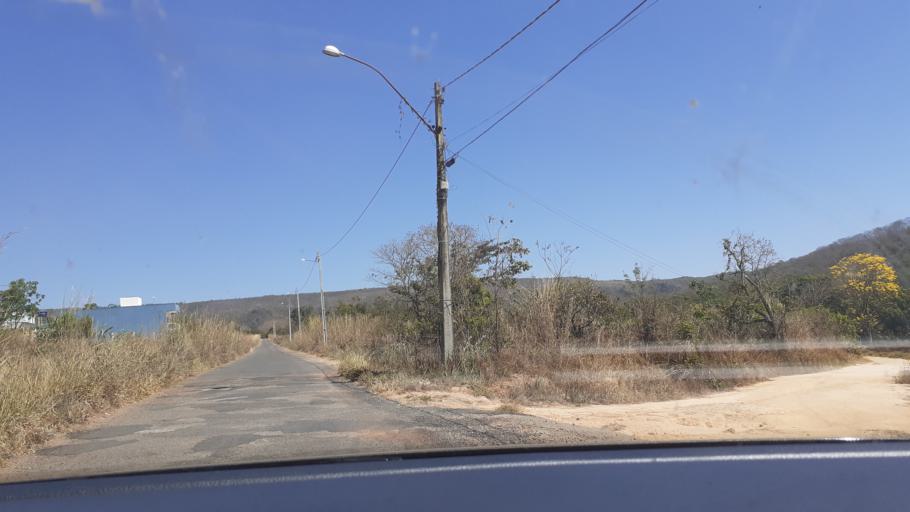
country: BR
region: Goias
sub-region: Caldas Novas
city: Caldas Novas
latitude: -17.7403
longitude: -48.6540
